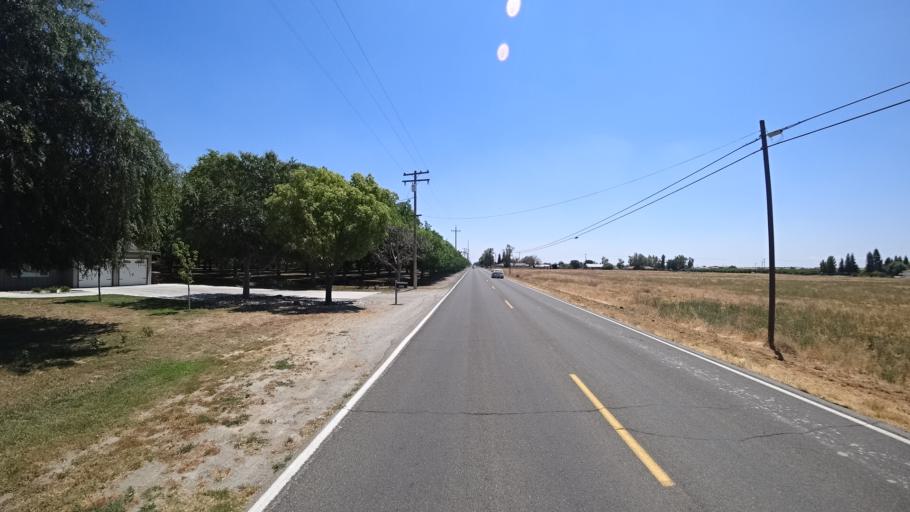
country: US
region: California
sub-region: Kings County
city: Lucerne
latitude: 36.3748
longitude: -119.6551
